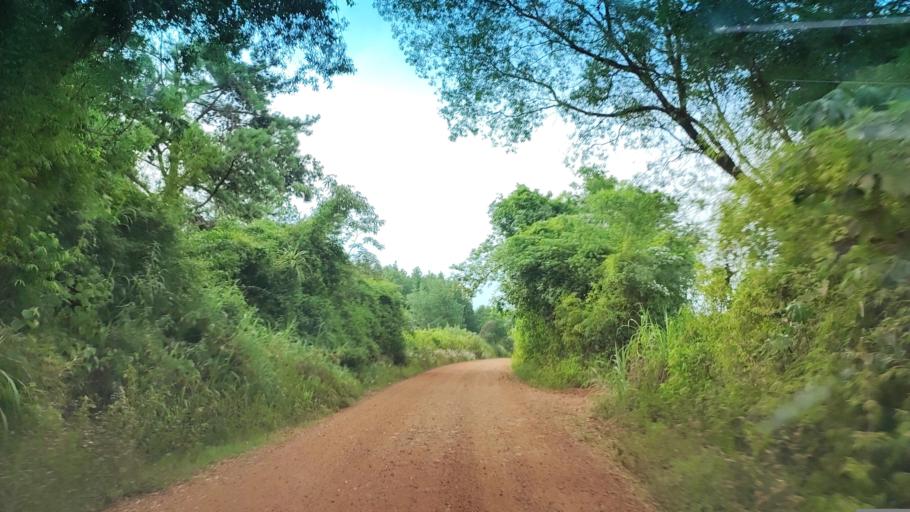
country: AR
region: Misiones
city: Gobernador Roca
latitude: -27.1690
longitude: -55.5106
